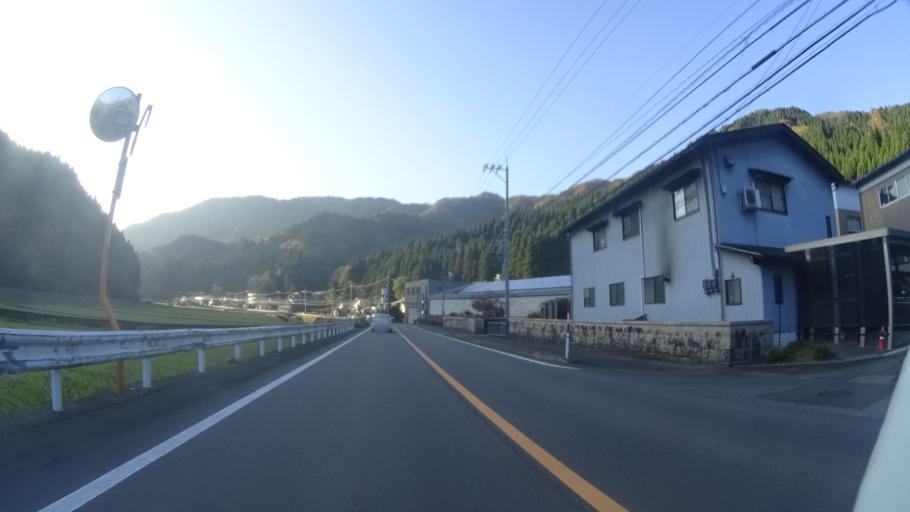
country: JP
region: Fukui
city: Ono
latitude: 36.0086
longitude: 136.3935
